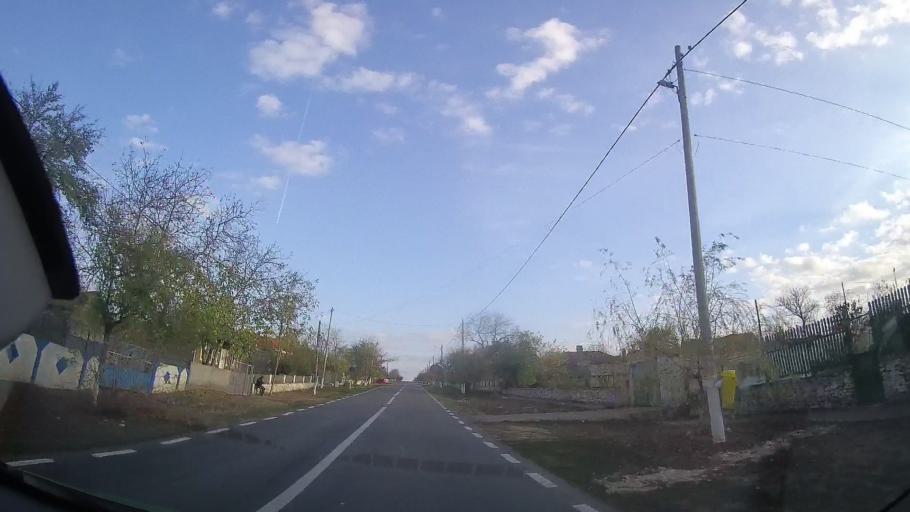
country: RO
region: Constanta
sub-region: Comuna Chirnogeni
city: Plopeni
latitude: 43.9613
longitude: 28.1426
